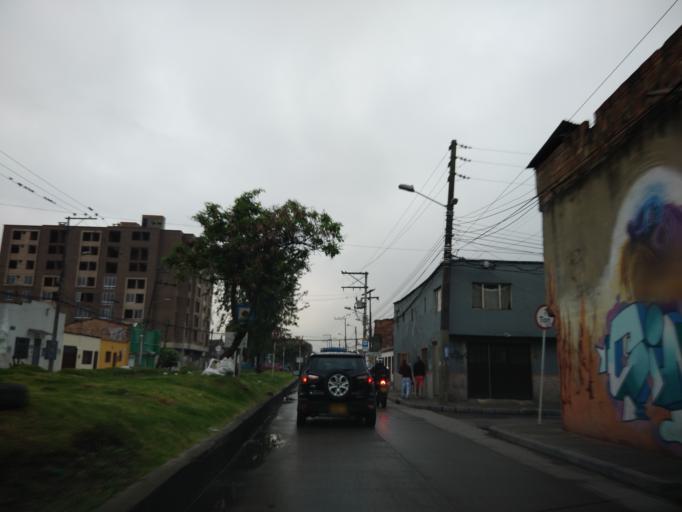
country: CO
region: Cundinamarca
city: Funza
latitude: 4.6787
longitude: -74.1430
